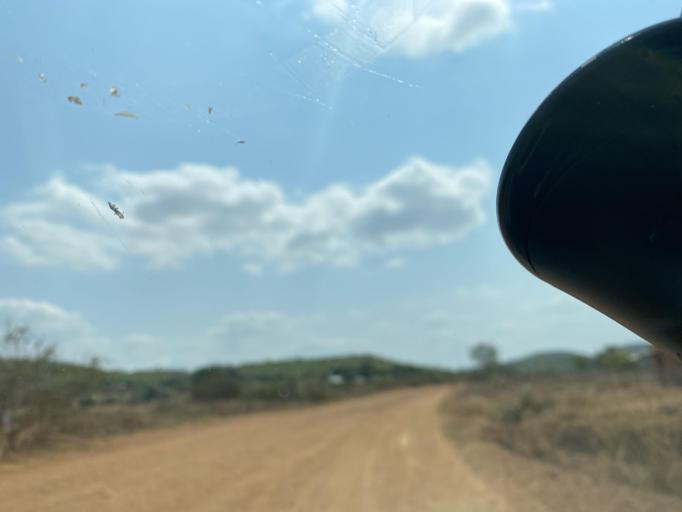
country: ZM
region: Lusaka
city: Chongwe
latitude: -15.6034
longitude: 28.7474
